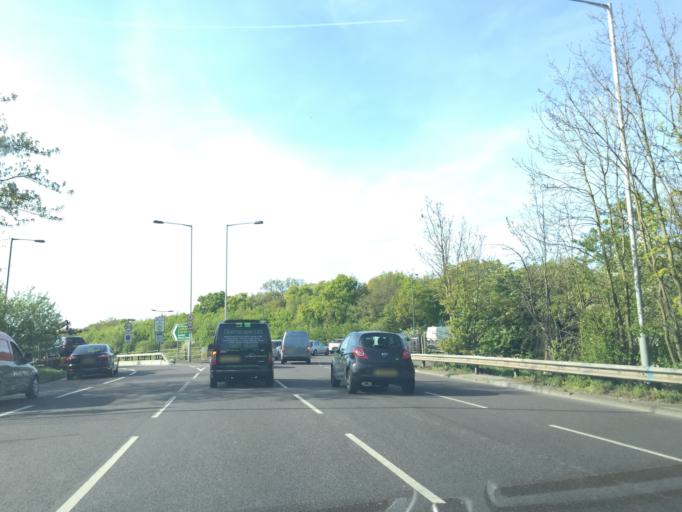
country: GB
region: England
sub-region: Greater London
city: Woodford Green
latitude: 51.5953
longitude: 0.0101
